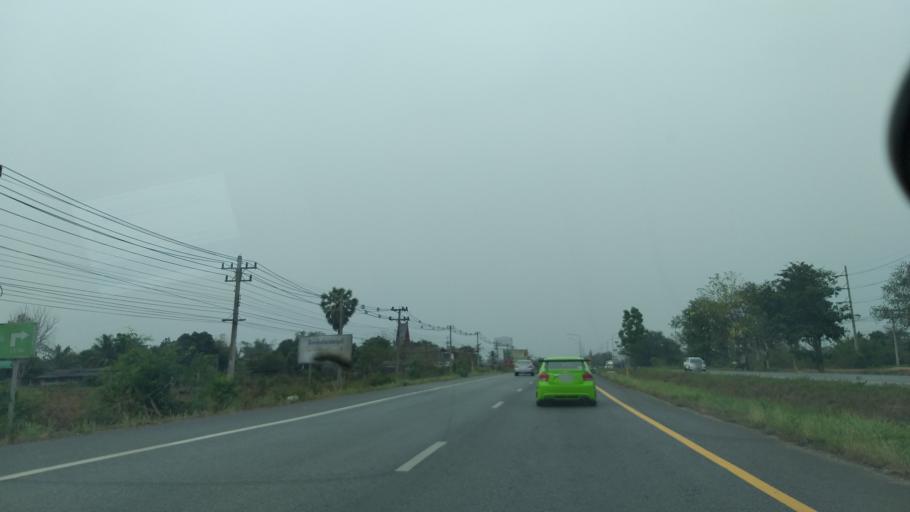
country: TH
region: Chon Buri
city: Ko Chan
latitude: 13.3521
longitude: 101.2712
